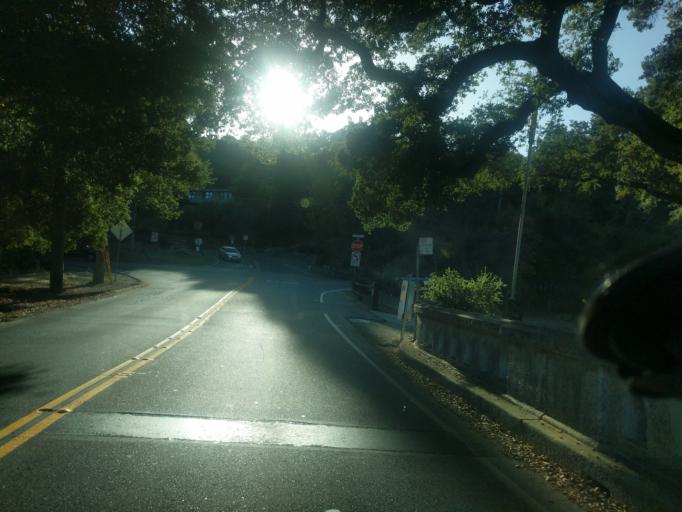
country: US
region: California
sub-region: Alameda County
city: Pleasanton
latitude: 37.6376
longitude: -121.8906
